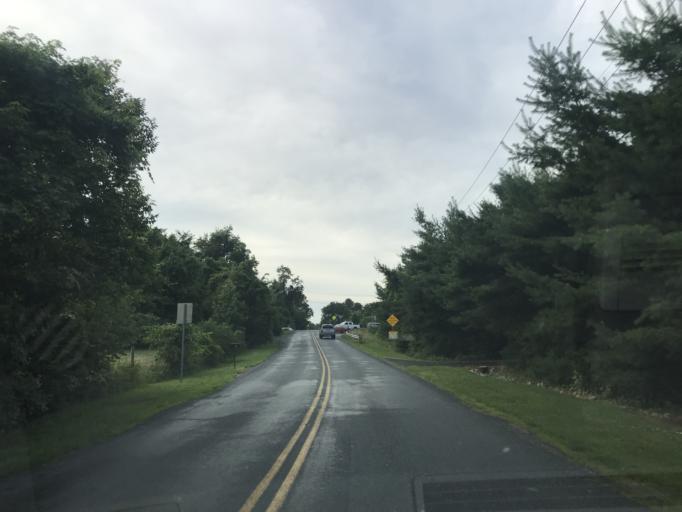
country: US
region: Maryland
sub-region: Harford County
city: Perryman
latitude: 39.5116
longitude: -76.2062
